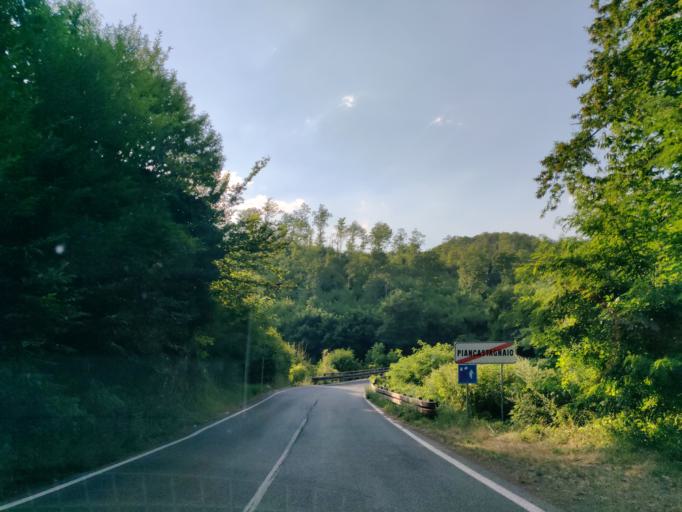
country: IT
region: Tuscany
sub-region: Provincia di Siena
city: Piancastagnaio
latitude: 42.8553
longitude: 11.6838
